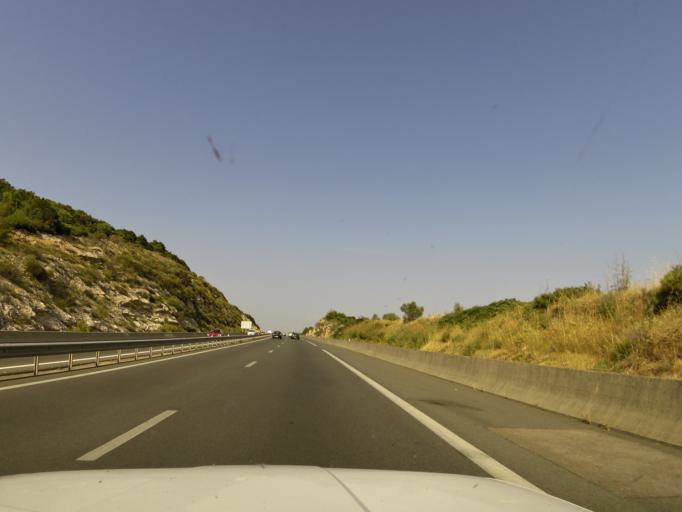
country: FR
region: Languedoc-Roussillon
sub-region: Departement de l'Herault
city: Montarnaud
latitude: 43.6269
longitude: 3.6663
